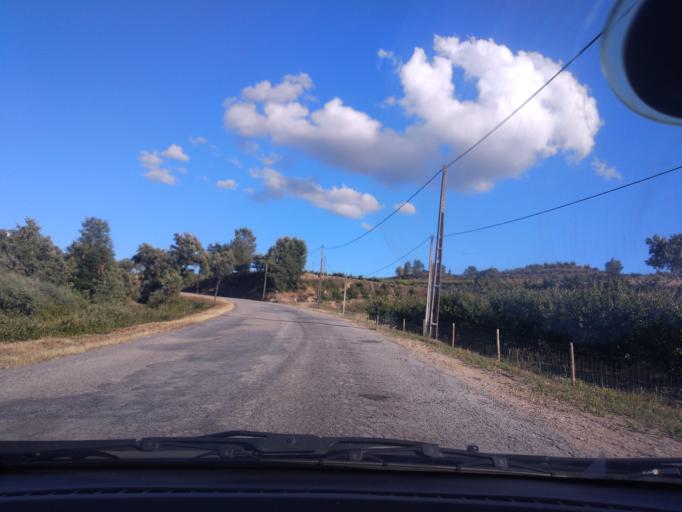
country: PT
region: Castelo Branco
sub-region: Covilha
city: Teixoso
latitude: 40.2372
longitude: -7.3853
